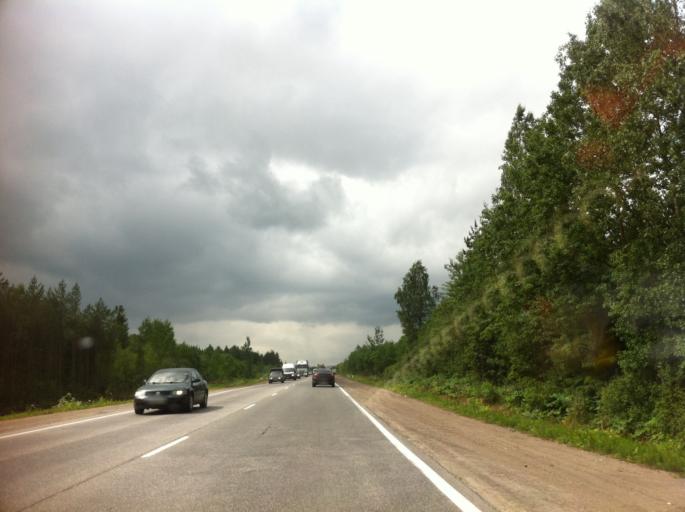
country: RU
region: Leningrad
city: Gatchina
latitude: 59.5264
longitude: 30.1031
